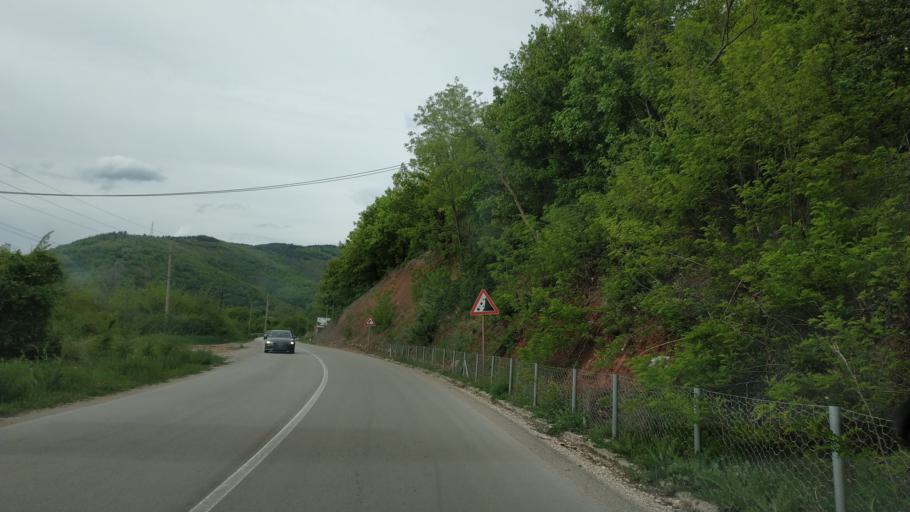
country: RS
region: Central Serbia
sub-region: Nisavski Okrug
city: Aleksinac
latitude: 43.6428
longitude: 21.7137
